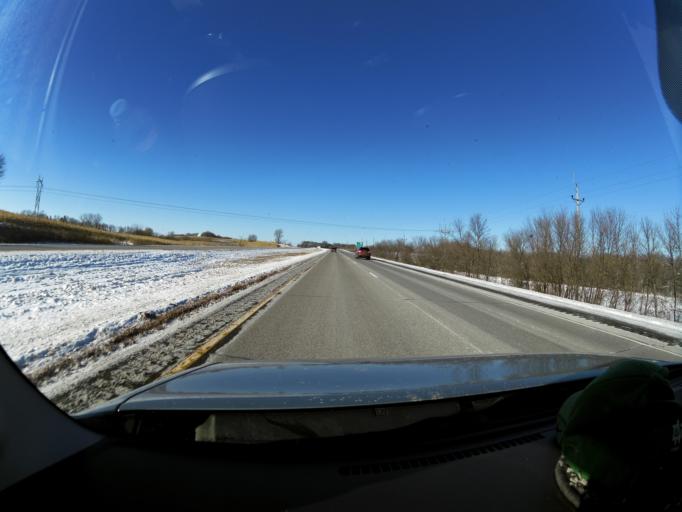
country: US
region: Minnesota
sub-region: Goodhue County
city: Zumbrota
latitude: 44.2716
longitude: -92.6552
